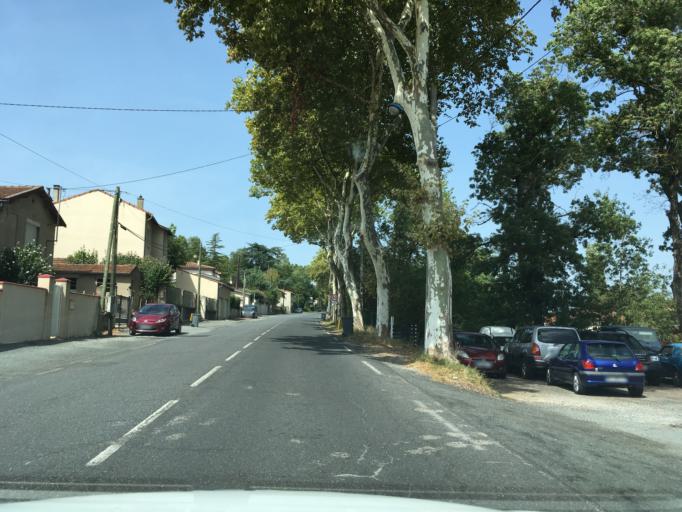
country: FR
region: Midi-Pyrenees
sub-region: Departement du Tarn
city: Castres
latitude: 43.6112
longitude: 2.2249
